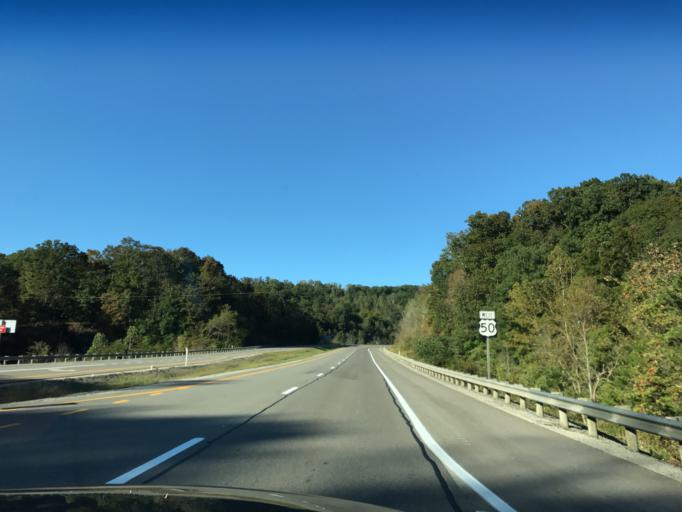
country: US
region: Ohio
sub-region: Washington County
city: Reno
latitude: 39.2423
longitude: -81.4002
